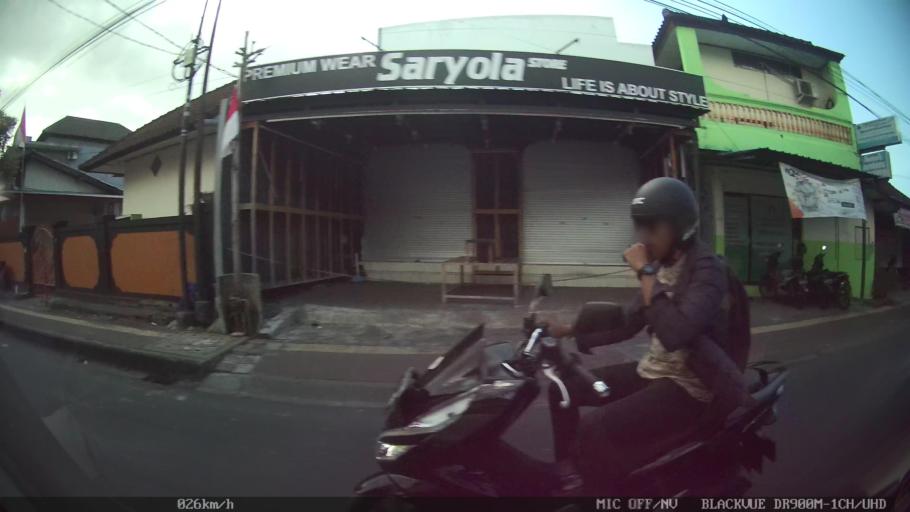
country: ID
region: Bali
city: Karyadharma
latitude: -8.6963
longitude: 115.1970
